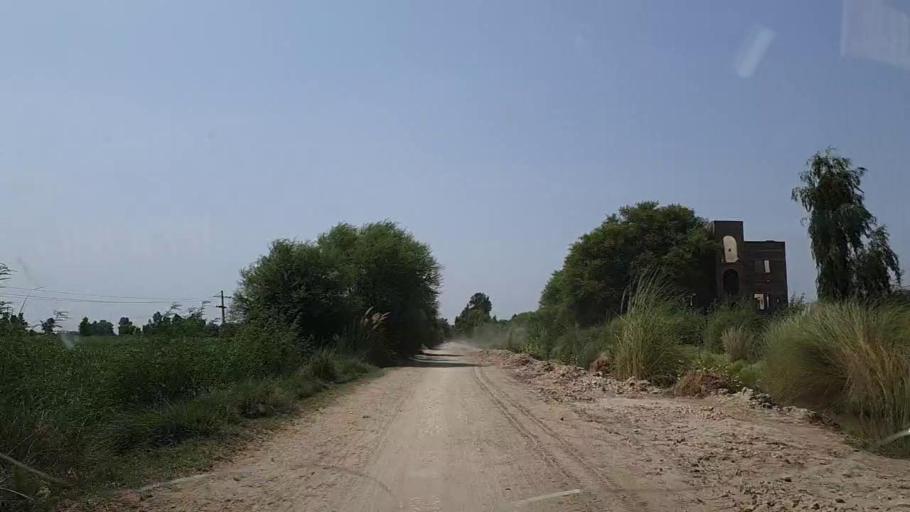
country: PK
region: Sindh
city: Ghotki
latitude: 28.0865
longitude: 69.3378
